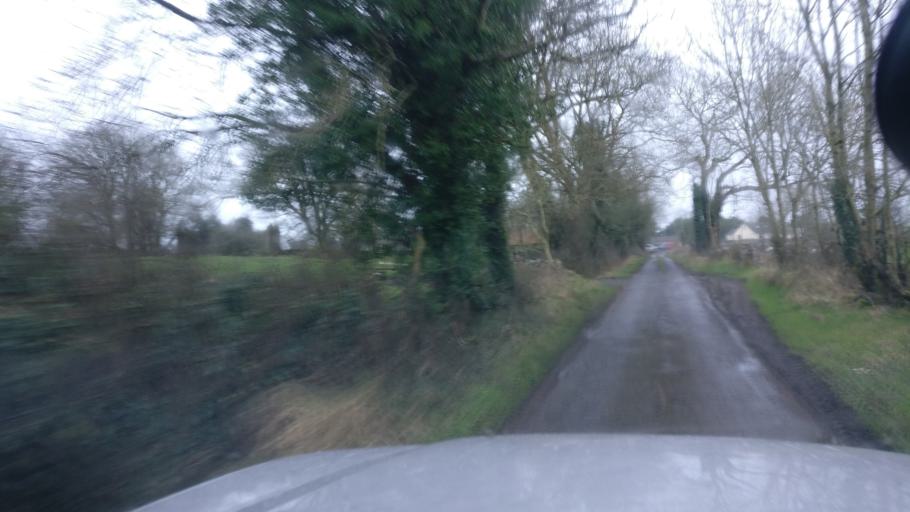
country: IE
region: Connaught
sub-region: County Galway
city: Loughrea
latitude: 53.2220
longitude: -8.5880
